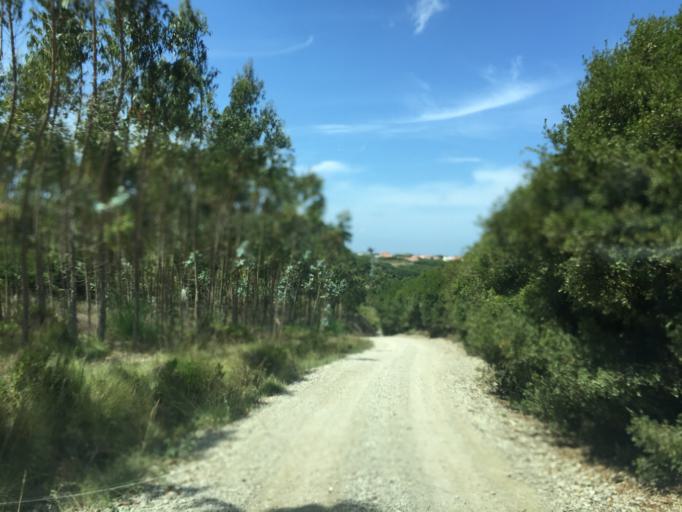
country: PT
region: Leiria
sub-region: Peniche
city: Atouguia da Baleia
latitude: 39.3231
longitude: -9.2622
